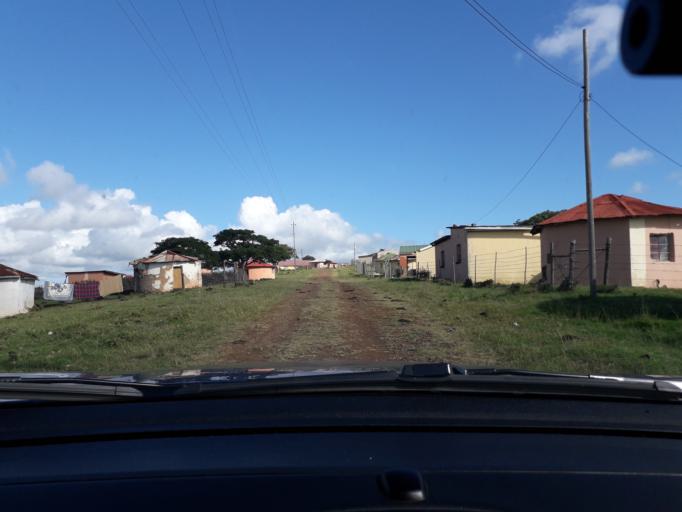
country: ZA
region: Eastern Cape
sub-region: Buffalo City Metropolitan Municipality
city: Bhisho
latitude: -33.1101
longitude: 27.4282
